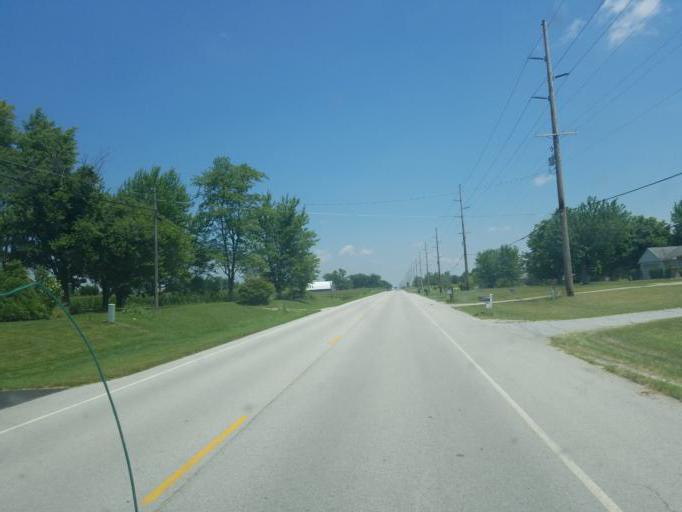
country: US
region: Ohio
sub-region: Auglaize County
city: Saint Marys
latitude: 40.5505
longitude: -84.3366
